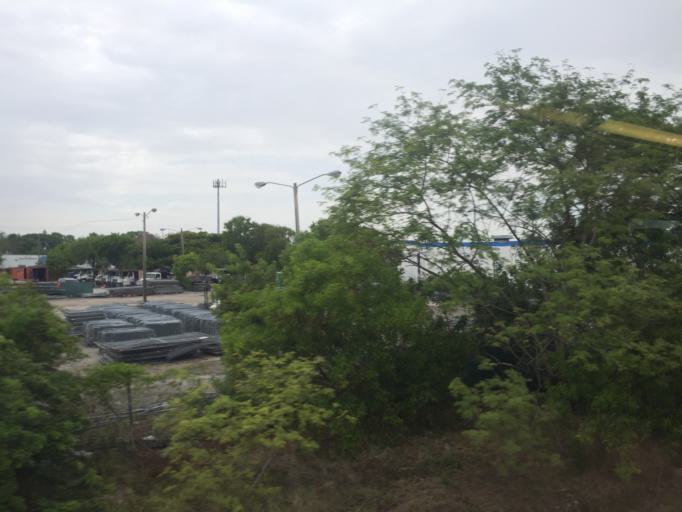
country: US
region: Florida
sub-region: Broward County
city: Dania Beach
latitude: 26.0463
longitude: -80.1679
